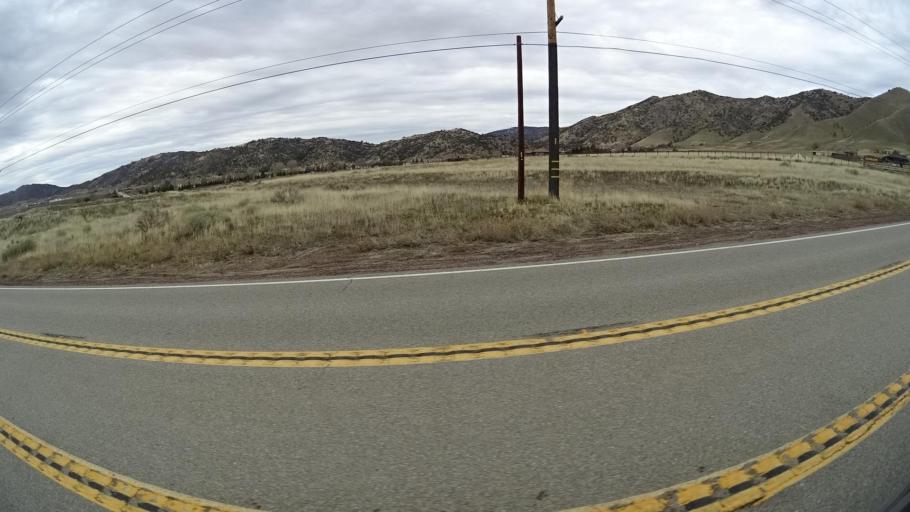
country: US
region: California
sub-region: Kern County
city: Bear Valley Springs
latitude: 35.1304
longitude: -118.5689
